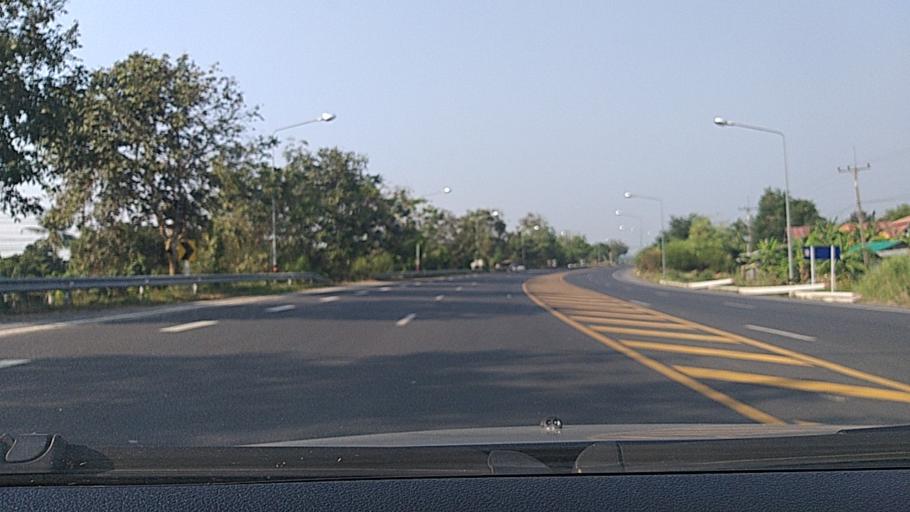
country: TH
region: Sing Buri
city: Phrom Buri
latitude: 14.7799
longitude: 100.4340
